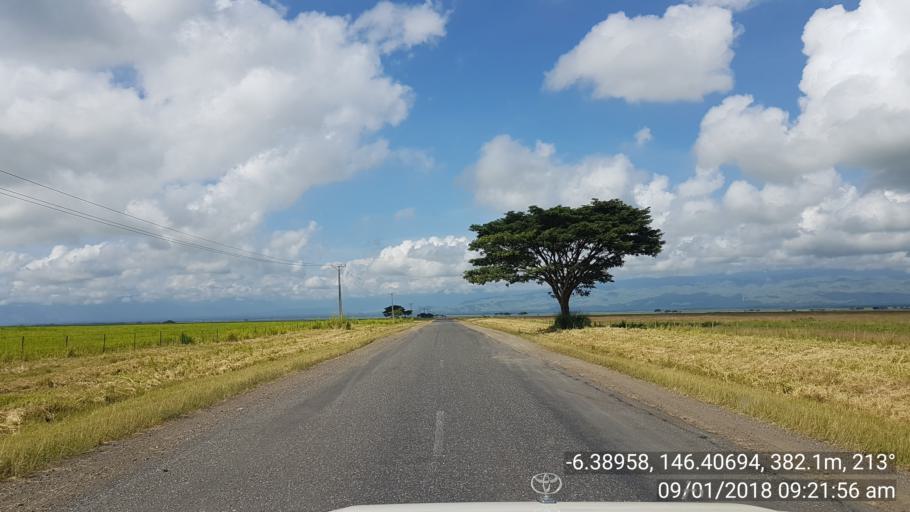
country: PG
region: Eastern Highlands
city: Kainantu
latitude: -6.3894
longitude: 146.4072
